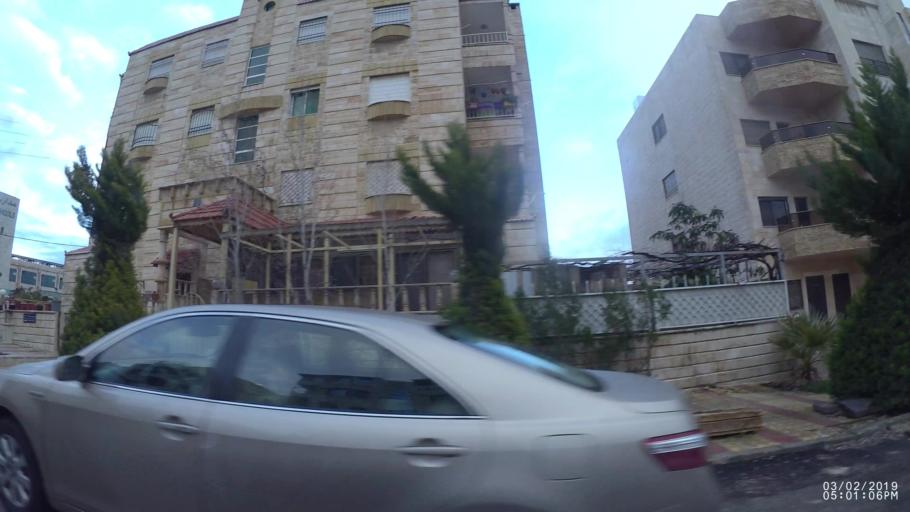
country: JO
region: Amman
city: Amman
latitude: 31.9808
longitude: 35.9152
